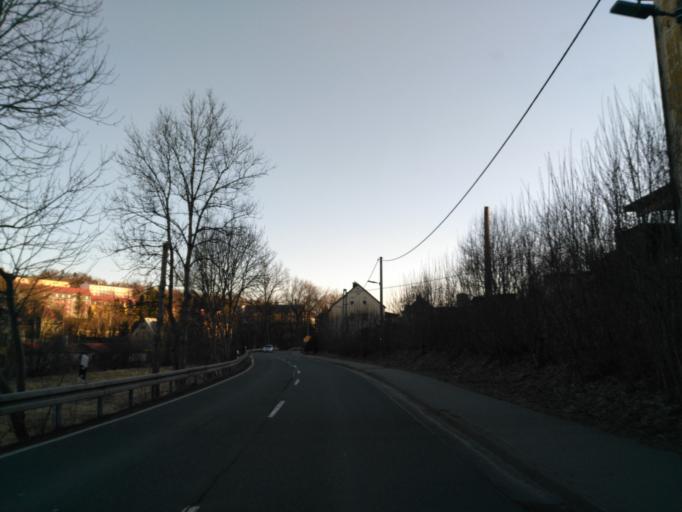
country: CZ
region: Ustecky
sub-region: Okres Chomutov
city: Vejprty
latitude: 50.4948
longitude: 13.0275
